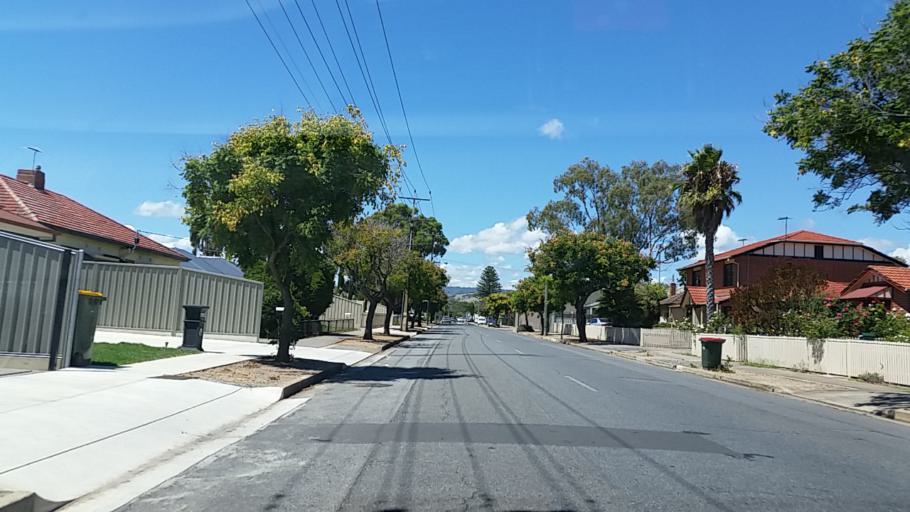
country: AU
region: South Australia
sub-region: Marion
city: Clovelly Park
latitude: -34.9868
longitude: 138.5669
